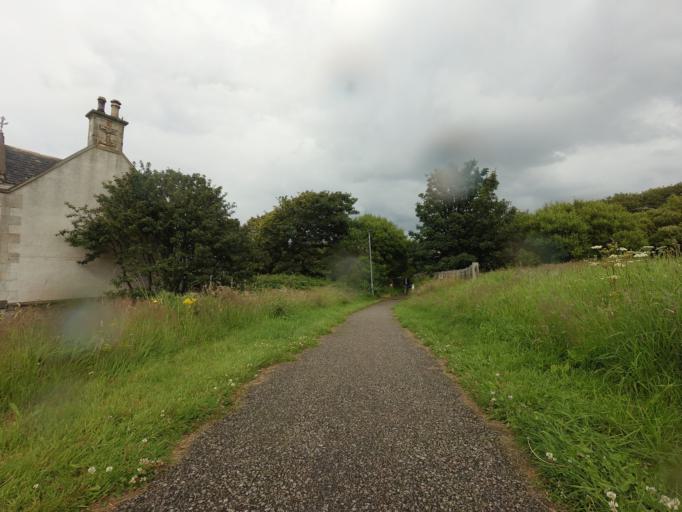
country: GB
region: Scotland
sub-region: Moray
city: Buckie
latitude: 57.6756
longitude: -2.9750
